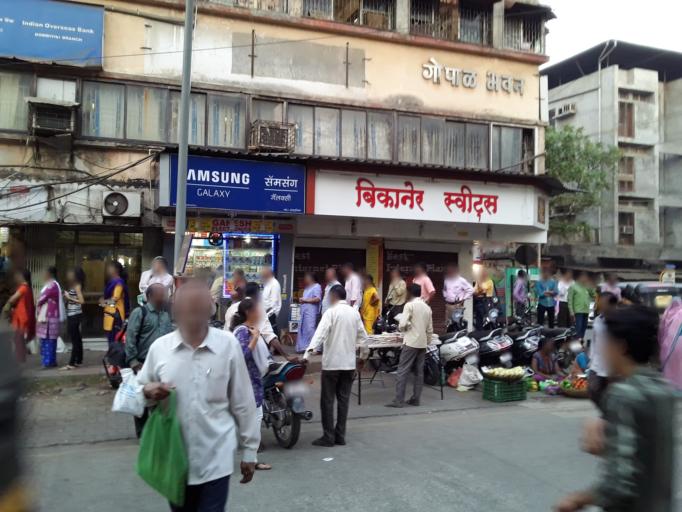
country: IN
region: Maharashtra
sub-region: Thane
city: Dombivli
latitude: 19.2163
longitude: 73.0870
